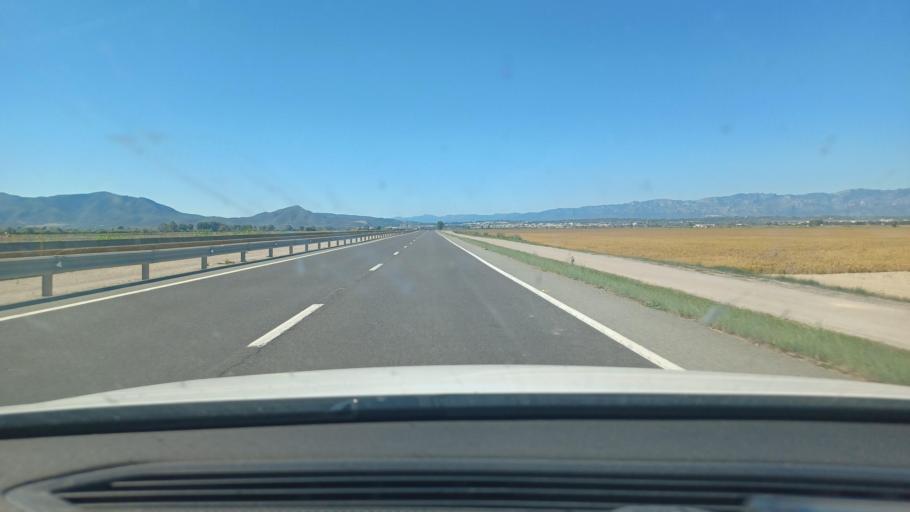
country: ES
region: Catalonia
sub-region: Provincia de Tarragona
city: Amposta
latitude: 40.7168
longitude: 0.6345
